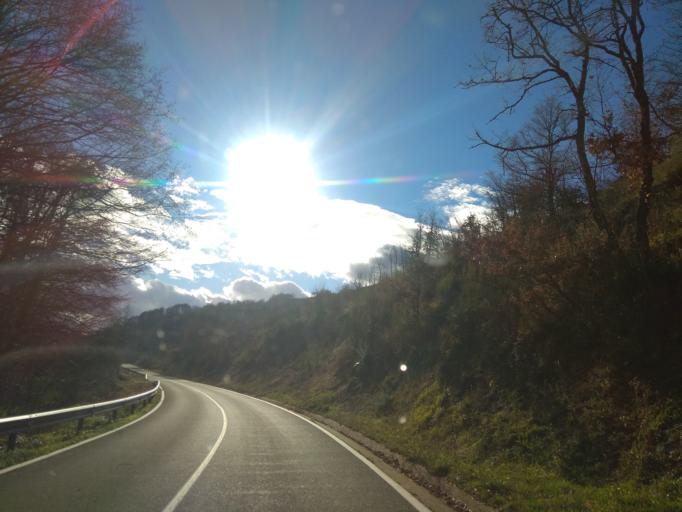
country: ES
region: Cantabria
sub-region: Provincia de Cantabria
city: San Martin de Elines
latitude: 42.8897
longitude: -3.9097
